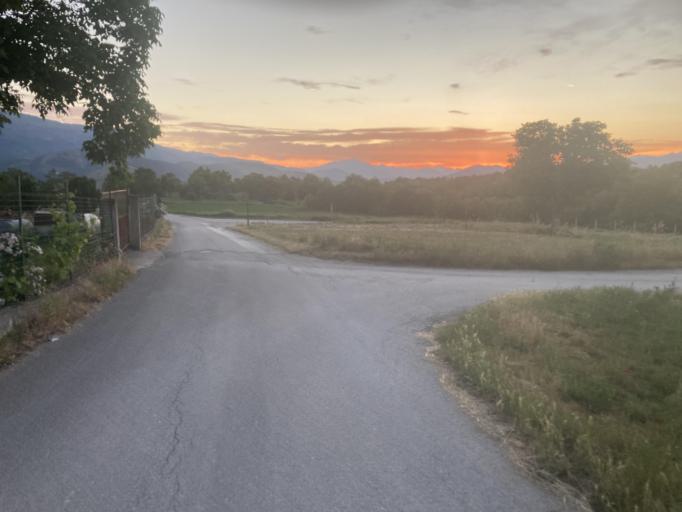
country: IT
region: Abruzzo
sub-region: Provincia dell' Aquila
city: San Demetrio Ne' Vestini
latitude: 42.2947
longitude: 13.5543
